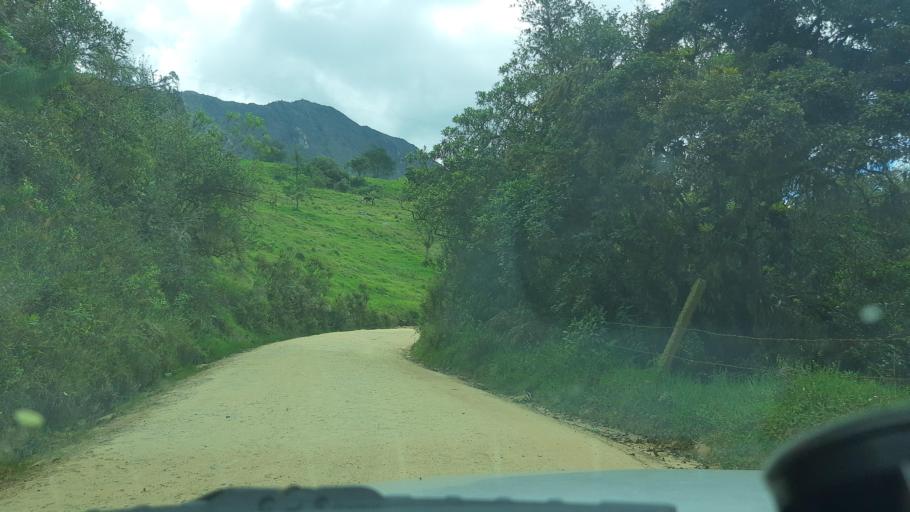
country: CO
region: Cundinamarca
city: Umbita
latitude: 5.2198
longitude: -73.4492
